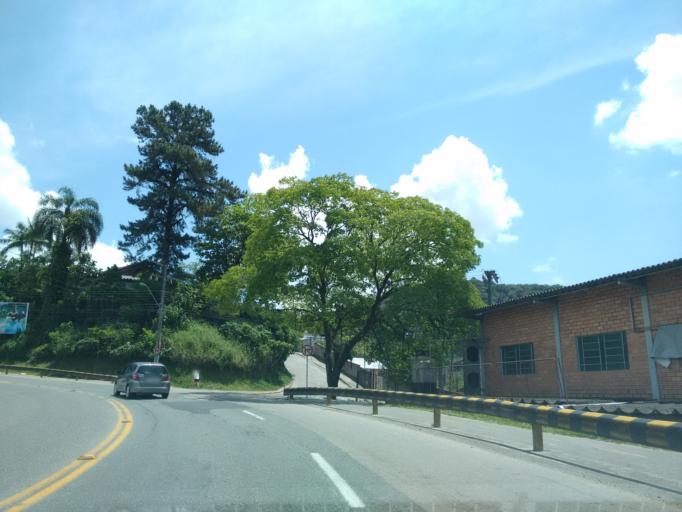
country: BR
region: Santa Catarina
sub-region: Blumenau
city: Blumenau
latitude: -26.9007
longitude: -49.0462
